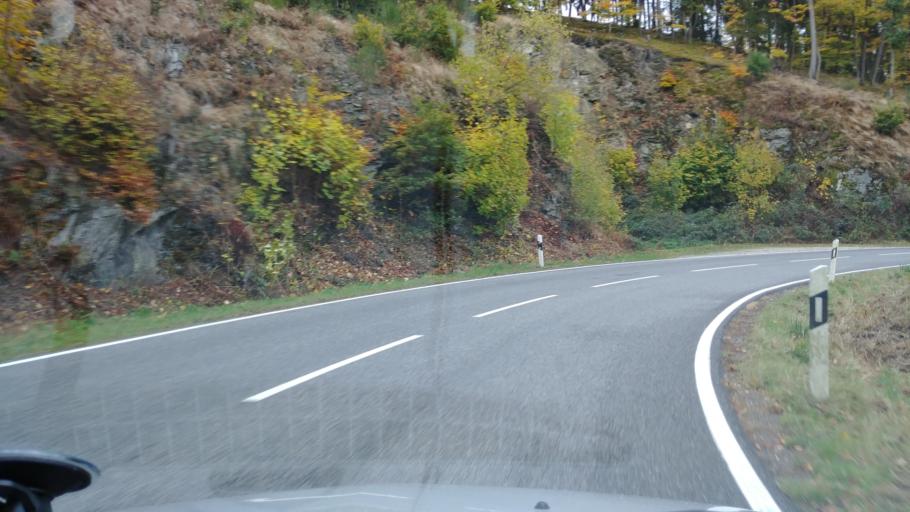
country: DE
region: Hesse
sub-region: Regierungsbezirk Darmstadt
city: Bad Schwalbach
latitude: 50.1381
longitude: 8.0535
